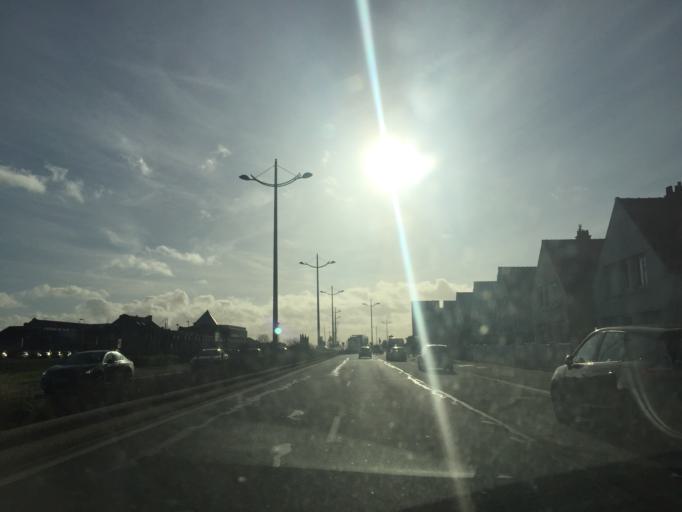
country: FR
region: Nord-Pas-de-Calais
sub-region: Departement du Pas-de-Calais
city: Calais
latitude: 50.9476
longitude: 1.8381
